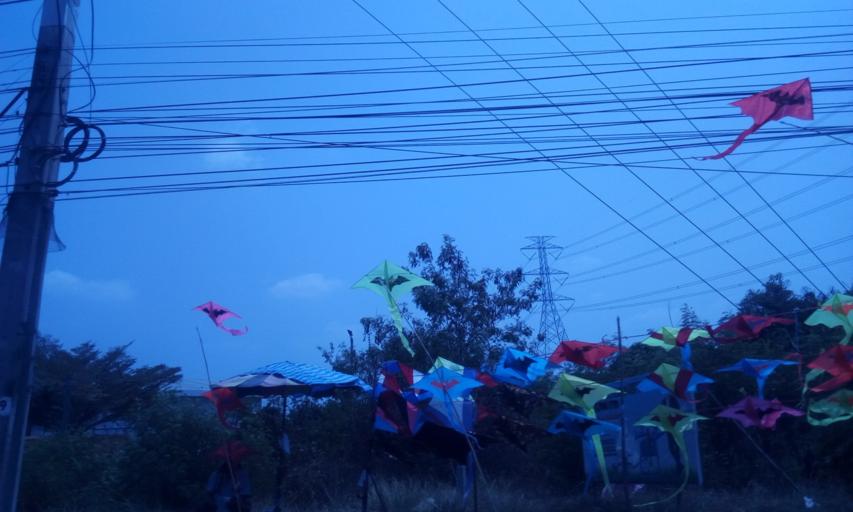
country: TH
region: Chachoengsao
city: Bang Nam Priao
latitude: 13.8264
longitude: 101.0550
